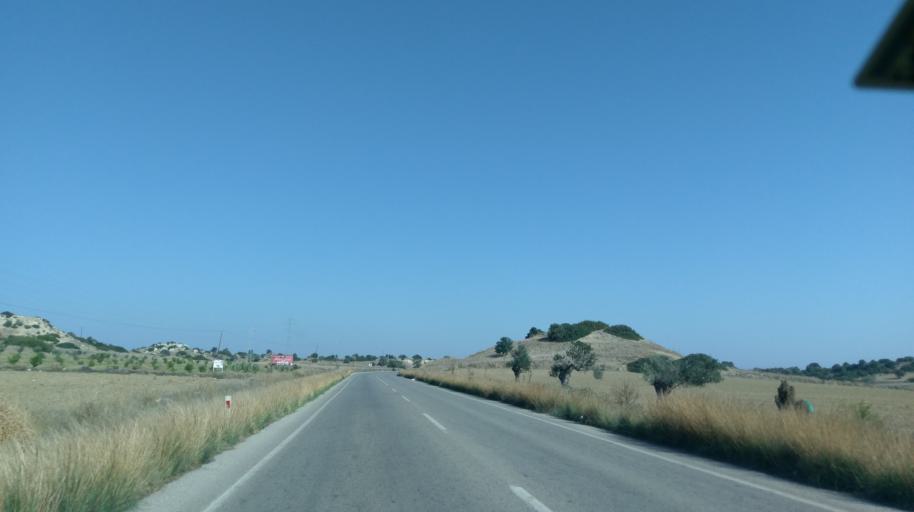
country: CY
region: Ammochostos
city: Leonarisso
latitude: 35.3869
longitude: 34.0512
